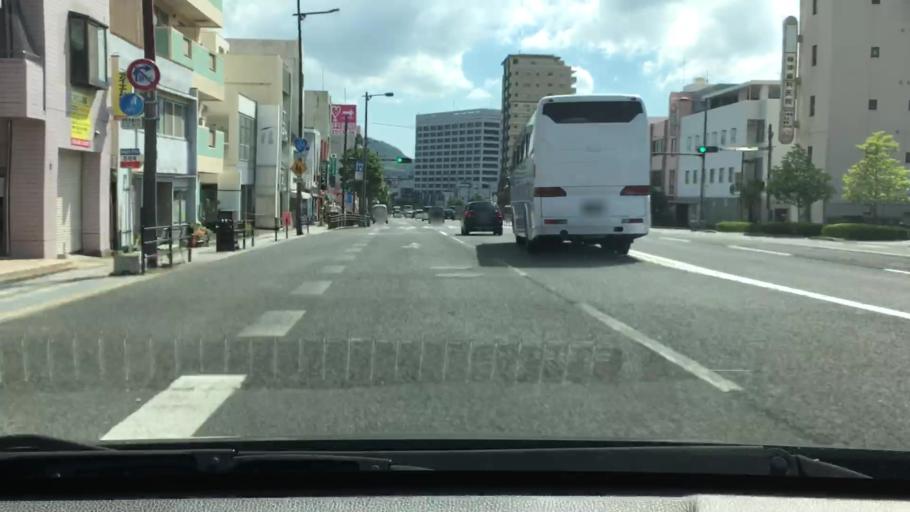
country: JP
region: Nagasaki
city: Sasebo
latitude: 33.1842
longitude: 129.7181
